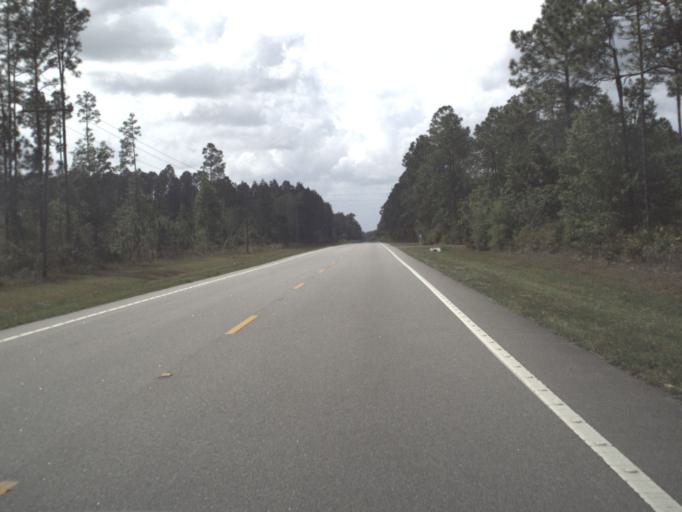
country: US
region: Florida
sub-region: Flagler County
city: Bunnell
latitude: 29.4714
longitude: -81.3215
